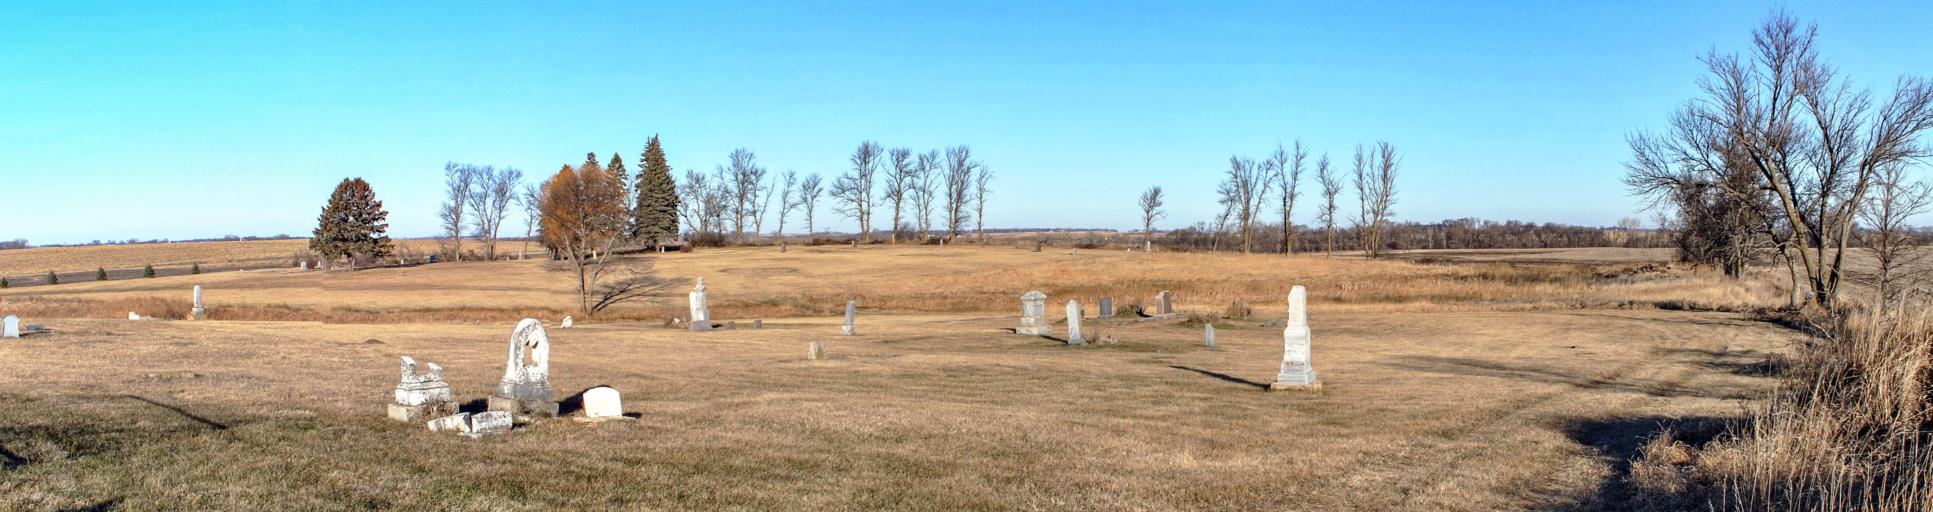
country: US
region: South Dakota
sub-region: Brookings County
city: Volga
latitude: 44.3332
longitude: -96.9445
